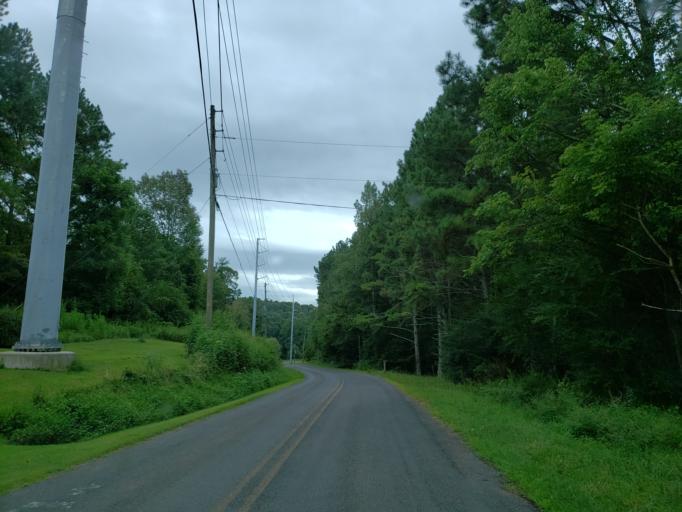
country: US
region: Georgia
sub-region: Gilmer County
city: Ellijay
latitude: 34.6145
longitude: -84.5686
